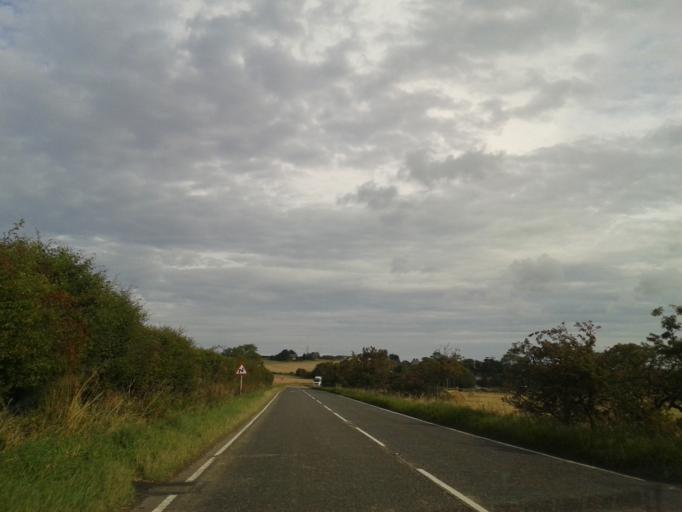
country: GB
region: Scotland
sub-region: Aberdeenshire
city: Whitehills
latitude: 57.6523
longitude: -2.6293
